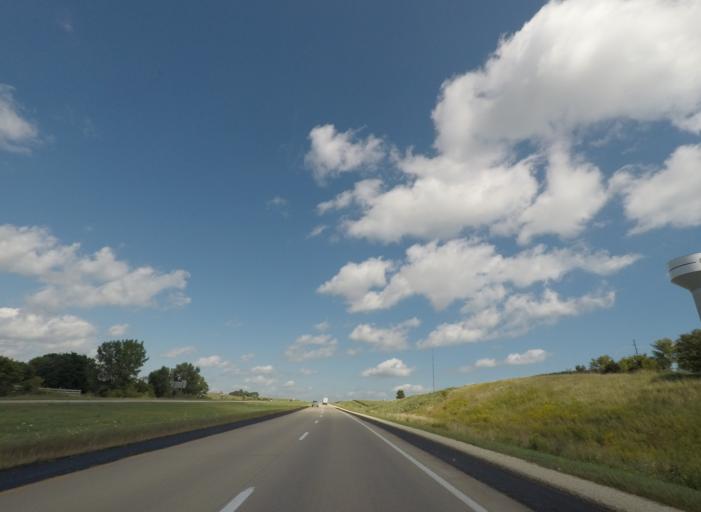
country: US
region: Iowa
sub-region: Dubuque County
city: Cascade
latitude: 42.3107
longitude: -90.9863
